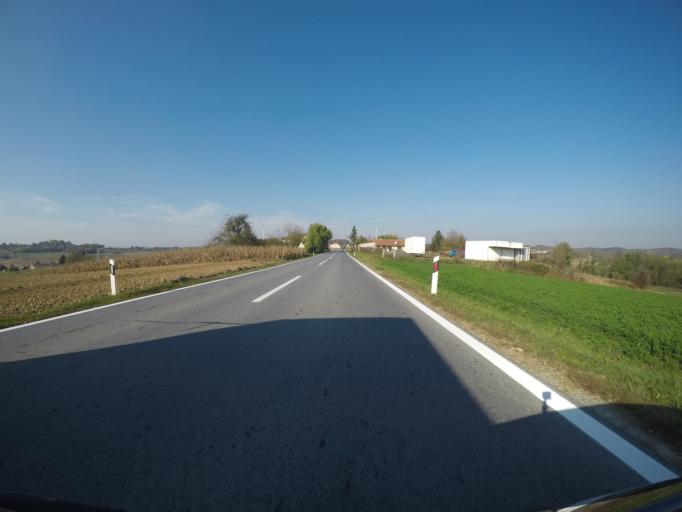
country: HR
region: Bjelovarsko-Bilogorska
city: Bjelovar
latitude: 45.9706
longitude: 16.8955
